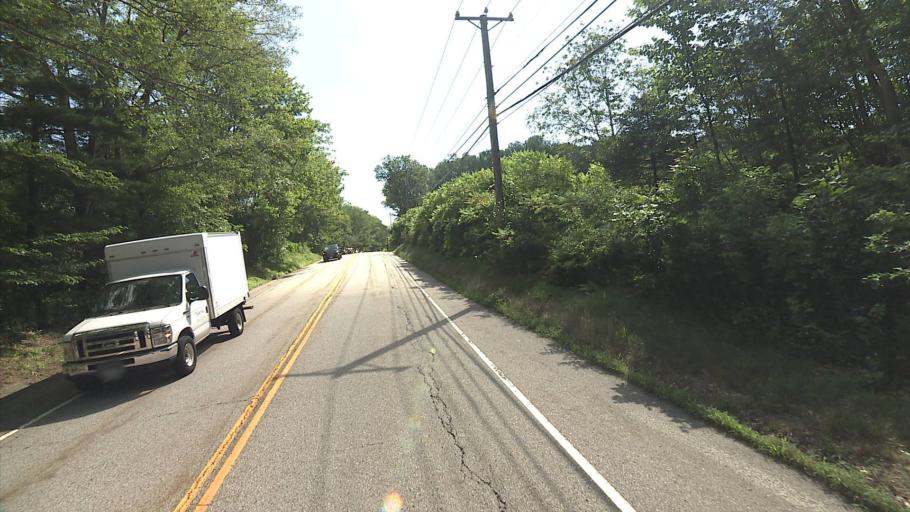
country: US
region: Connecticut
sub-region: Tolland County
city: Stafford
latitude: 41.9644
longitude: -72.2102
